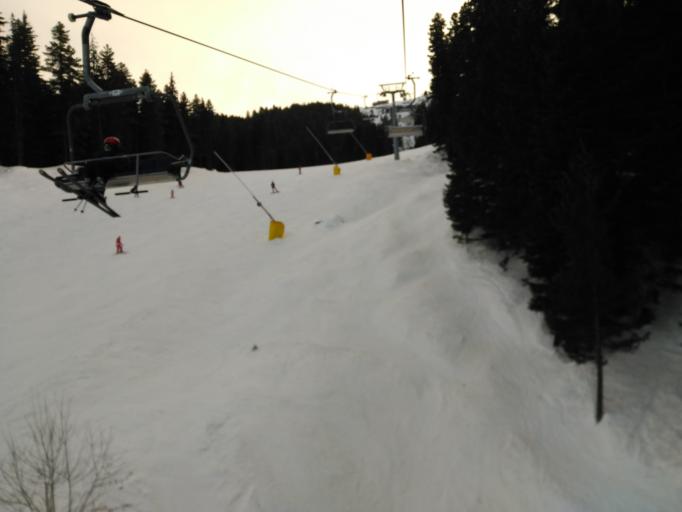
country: BG
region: Blagoevgrad
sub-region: Obshtina Bansko
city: Bansko
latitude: 41.7719
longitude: 23.4484
